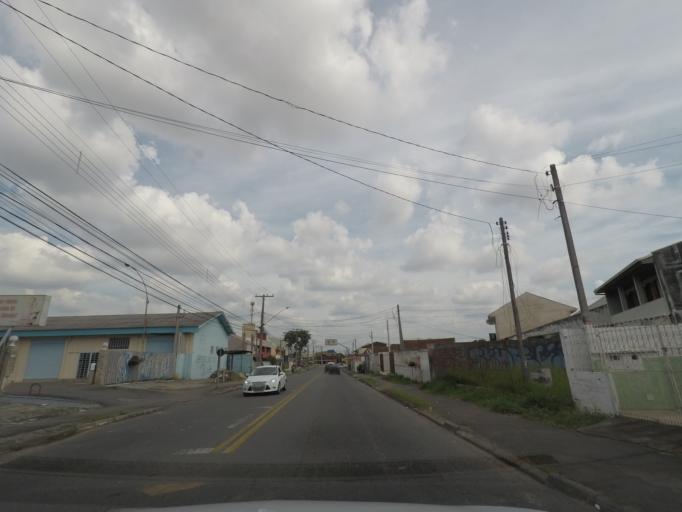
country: BR
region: Parana
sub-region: Sao Jose Dos Pinhais
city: Sao Jose dos Pinhais
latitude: -25.4952
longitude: -49.2161
